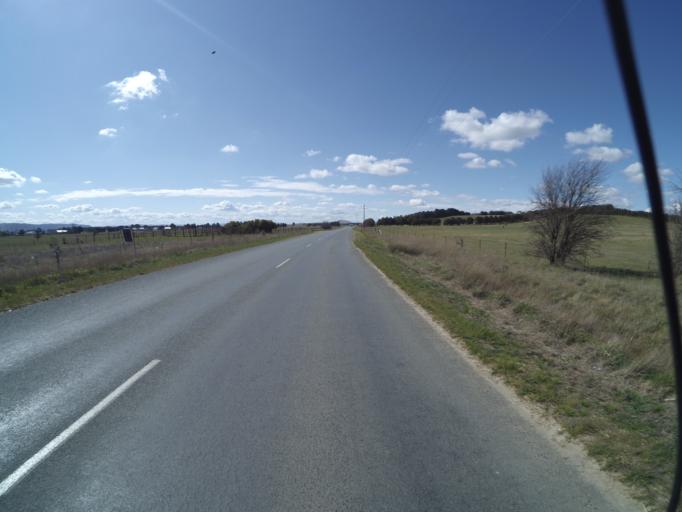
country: AU
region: New South Wales
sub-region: Palerang
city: Bungendore
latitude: -35.2355
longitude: 149.4446
